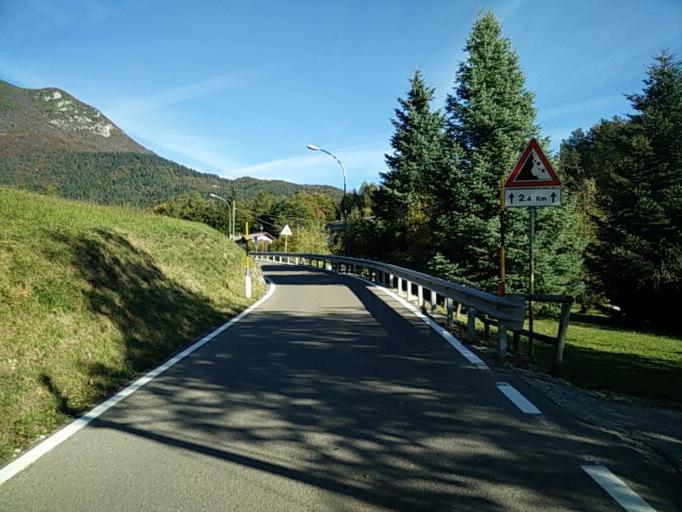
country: IT
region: Trentino-Alto Adige
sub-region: Provincia di Trento
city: Garniga Nuova
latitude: 46.0041
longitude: 11.0859
